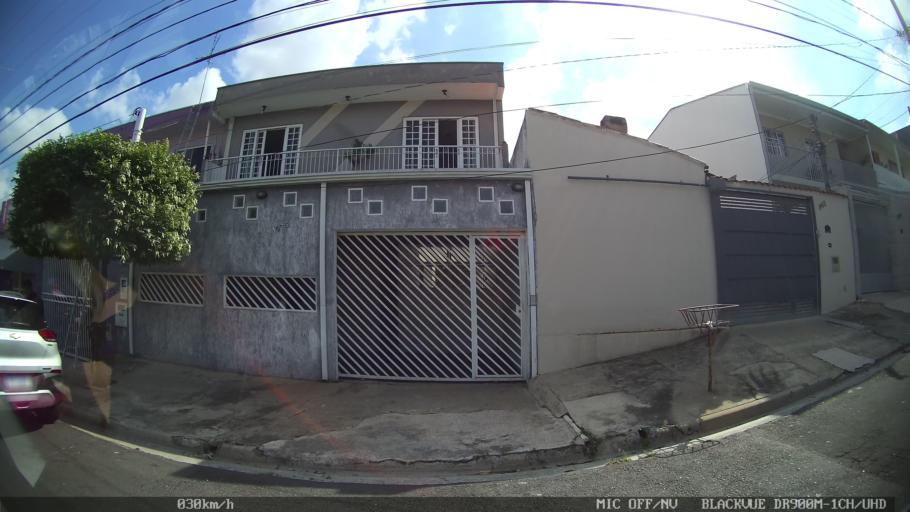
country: BR
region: Sao Paulo
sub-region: Campinas
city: Campinas
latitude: -22.9401
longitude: -47.1206
